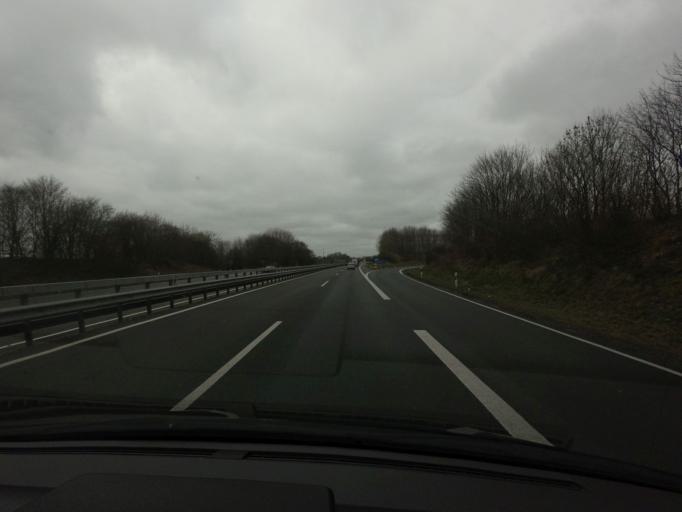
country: DE
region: Lower Saxony
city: Westerstede
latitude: 53.2593
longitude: 7.9422
